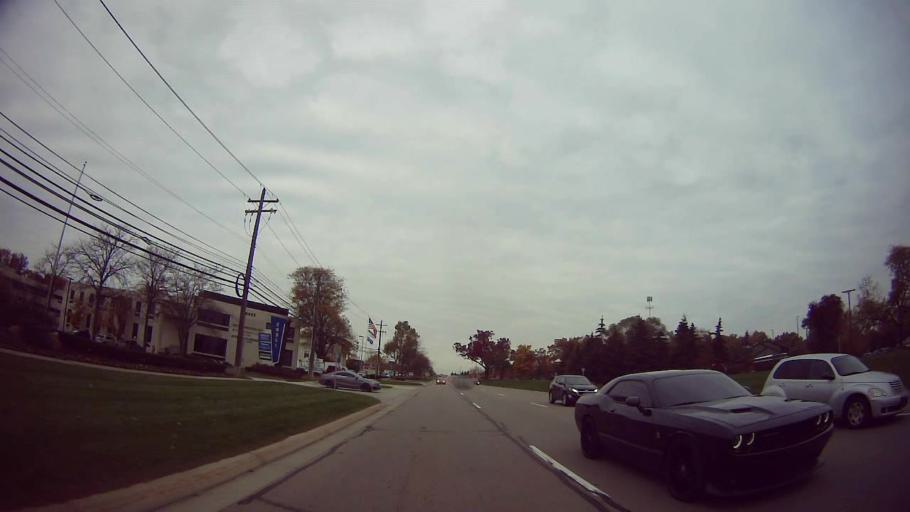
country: US
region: Michigan
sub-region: Oakland County
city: Franklin
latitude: 42.5034
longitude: -83.3135
